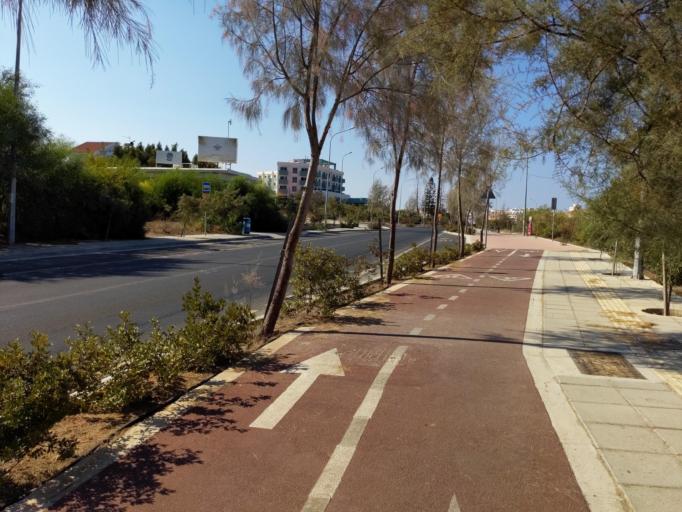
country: CY
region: Ammochostos
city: Protaras
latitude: 35.0282
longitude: 34.0385
